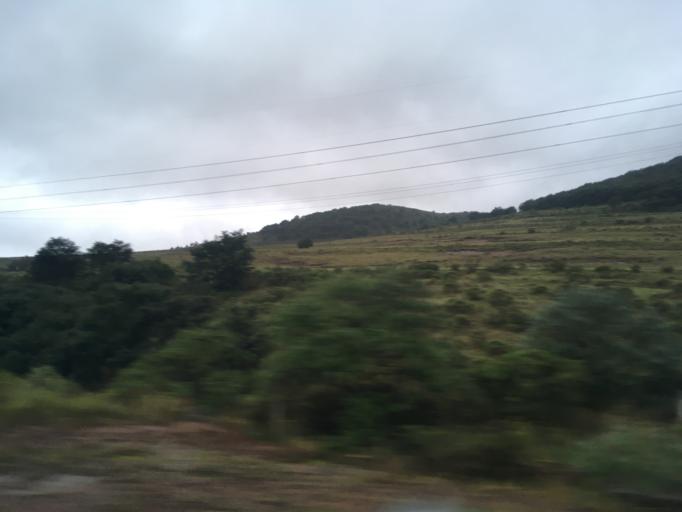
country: MX
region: Puebla
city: Chignahuapan
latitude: 19.8391
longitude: -98.0564
